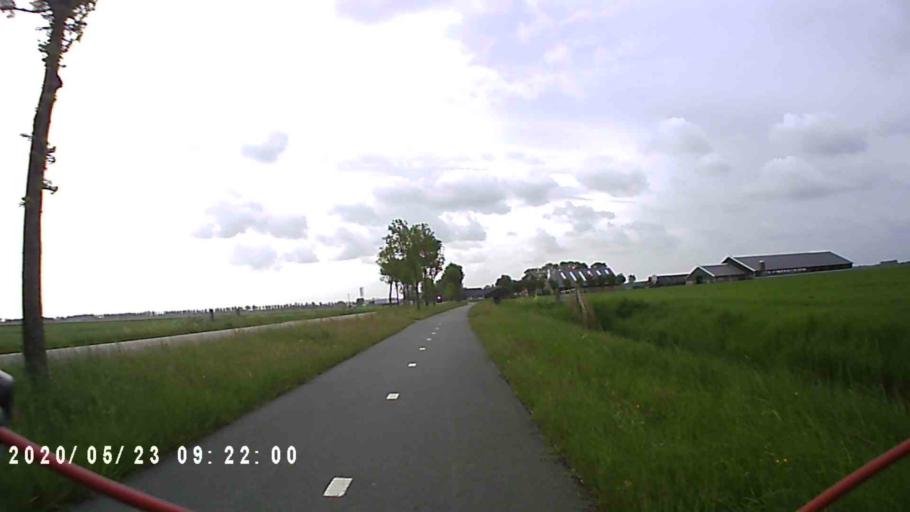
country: NL
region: Groningen
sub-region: Gemeente Bedum
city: Bedum
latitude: 53.2913
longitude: 6.6788
